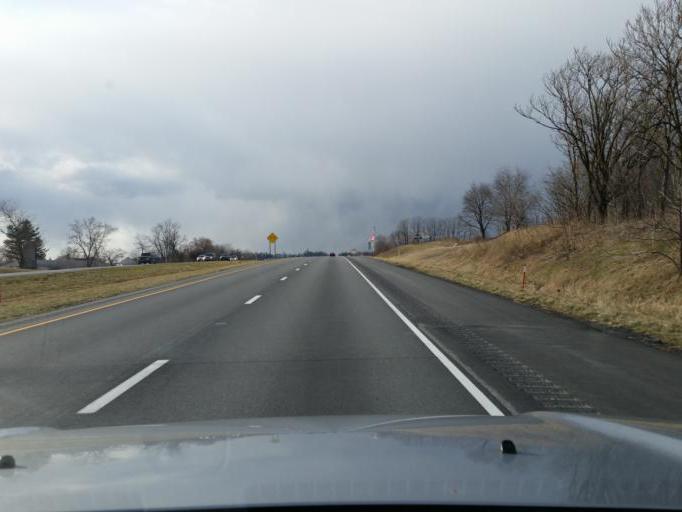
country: US
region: Pennsylvania
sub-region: Lancaster County
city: Rheems
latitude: 40.1374
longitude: -76.5474
